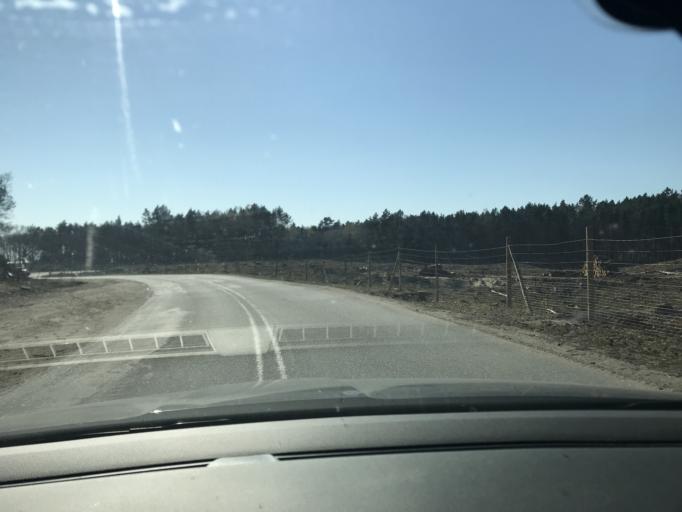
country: PL
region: Pomeranian Voivodeship
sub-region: Powiat nowodworski
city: Krynica Morska
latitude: 54.3555
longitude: 19.3144
